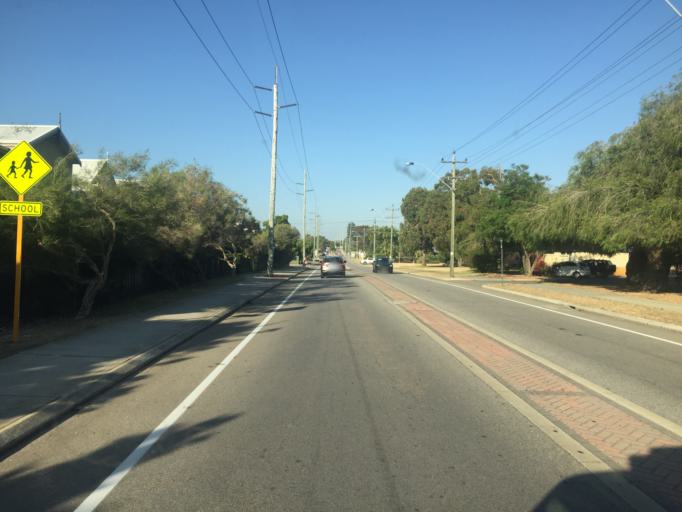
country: AU
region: Western Australia
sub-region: Belmont
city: Belmont
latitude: -31.9572
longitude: 115.9328
